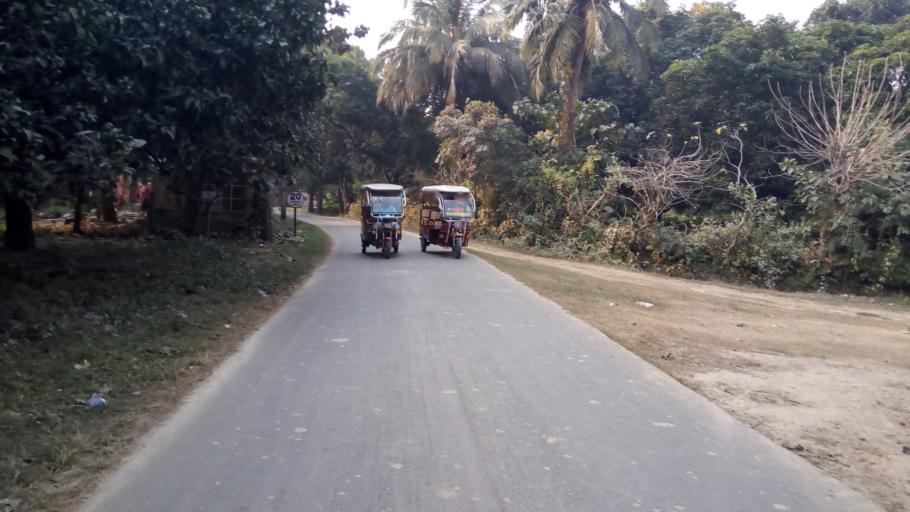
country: IN
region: West Bengal
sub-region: Nadia
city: Navadwip
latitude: 23.4475
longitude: 88.4174
